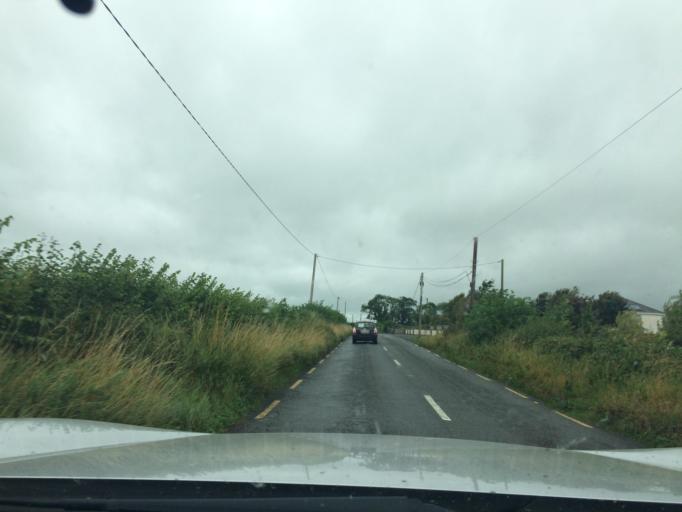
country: IE
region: Munster
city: Cashel
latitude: 52.4873
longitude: -7.8565
